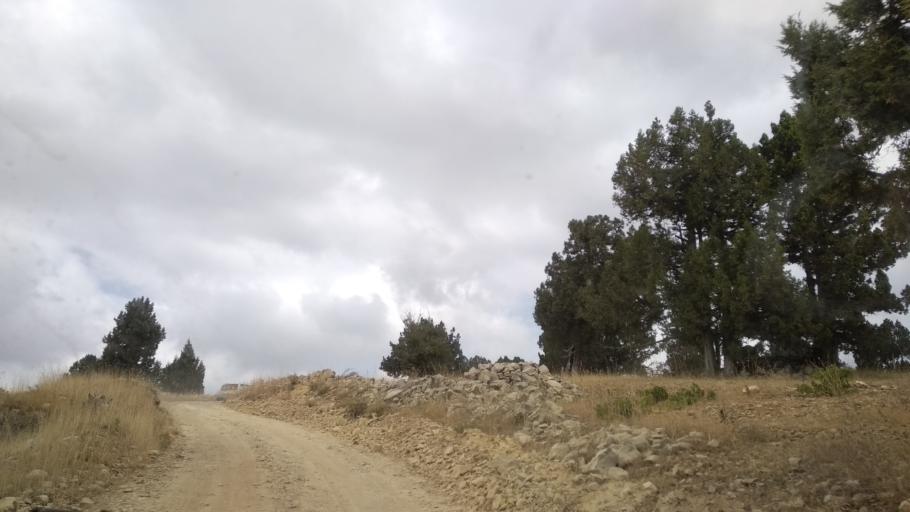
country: TR
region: Mersin
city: Sarikavak
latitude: 36.5658
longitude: 33.7666
